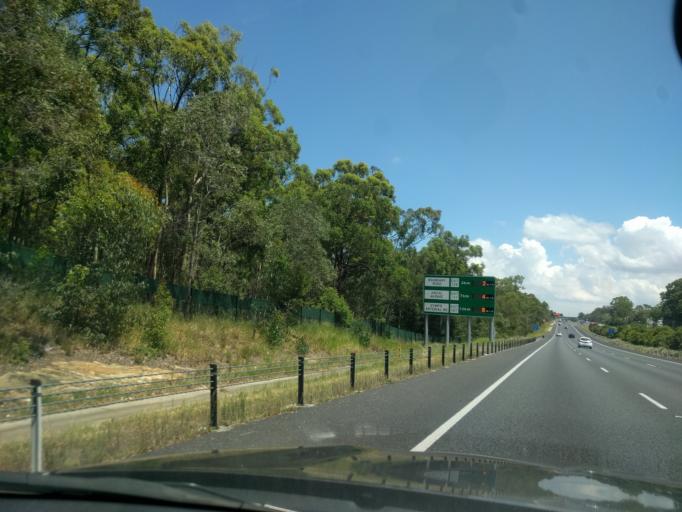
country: AU
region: Queensland
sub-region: Moreton Bay
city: Narangba
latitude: -27.1893
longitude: 152.9868
